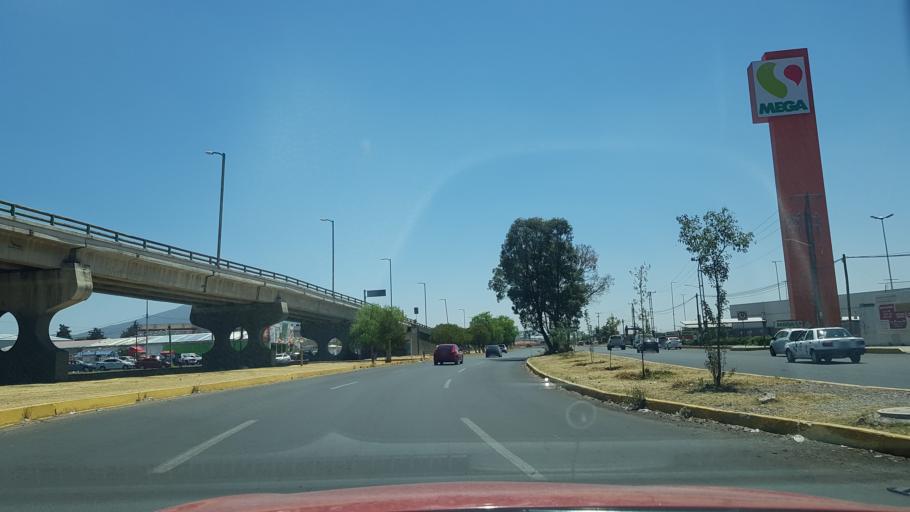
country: MX
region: Mexico
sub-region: Atlacomulco
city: Santa Cruz Bombatevi
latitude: 19.7929
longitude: -99.8874
